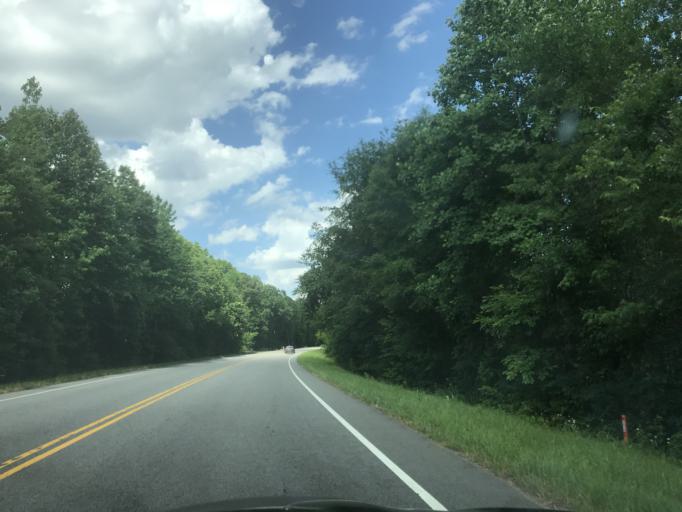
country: US
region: North Carolina
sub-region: Nash County
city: Spring Hope
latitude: 35.9295
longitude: -78.1460
